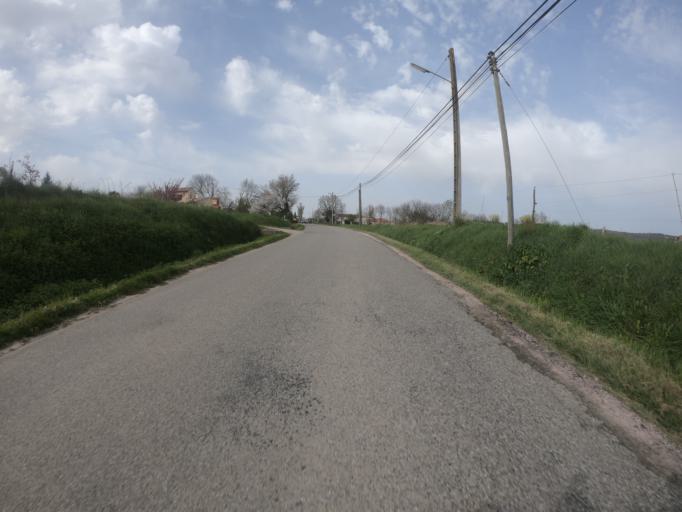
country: FR
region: Midi-Pyrenees
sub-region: Departement de l'Ariege
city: La Tour-du-Crieu
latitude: 43.1070
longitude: 1.7234
